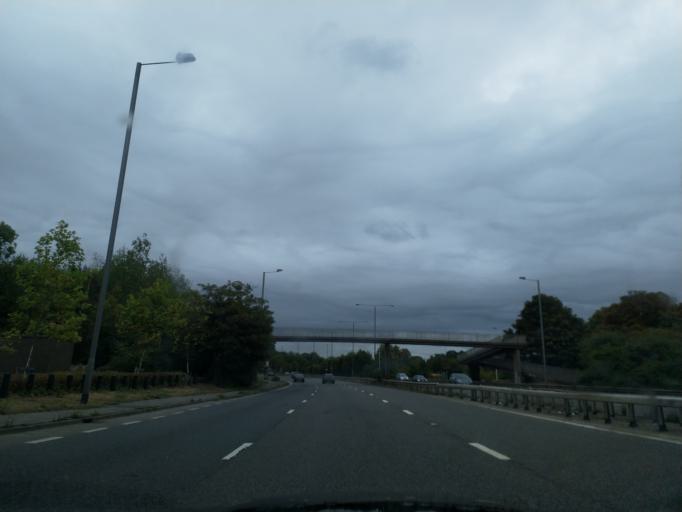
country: GB
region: England
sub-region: Surrey
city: Sunbury-on-Thames
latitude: 51.4218
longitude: -0.4122
